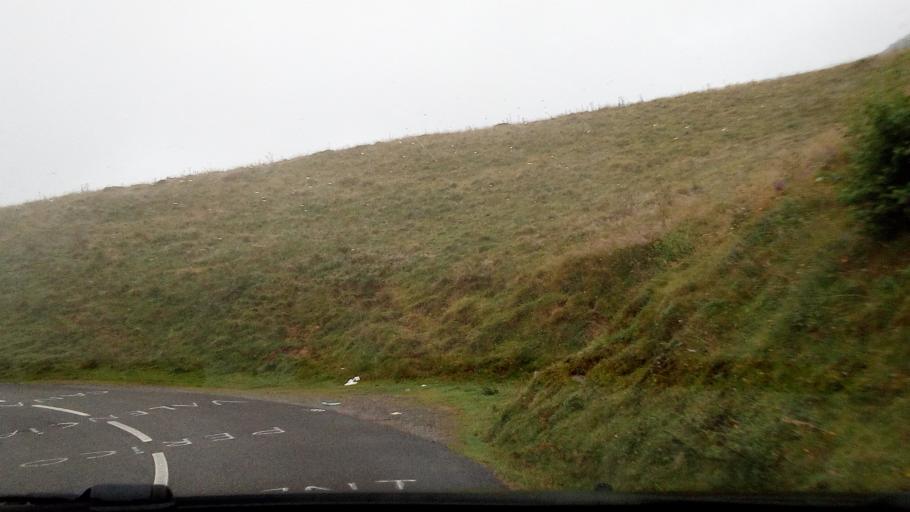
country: FR
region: Aquitaine
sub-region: Departement des Pyrenees-Atlantiques
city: Laruns
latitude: 42.9745
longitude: -0.3081
